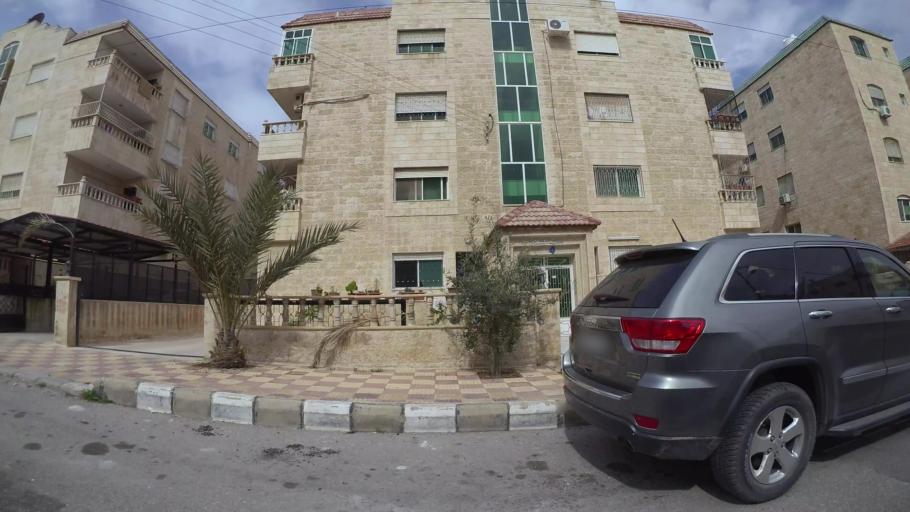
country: JO
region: Amman
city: Amman
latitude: 31.9952
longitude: 35.9420
